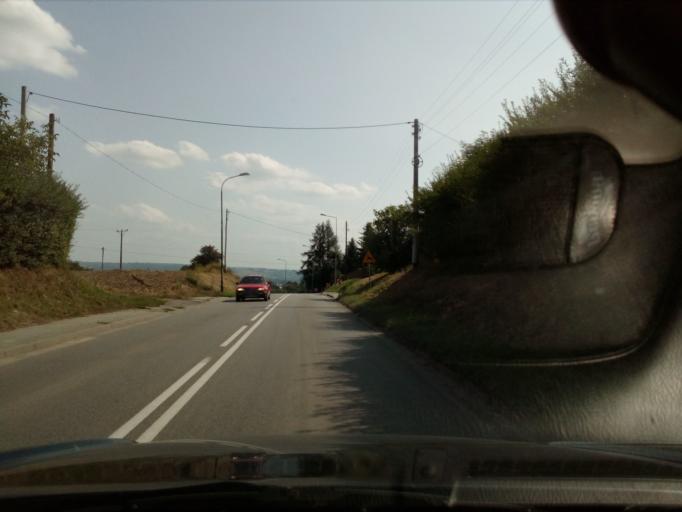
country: PL
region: Subcarpathian Voivodeship
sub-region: Powiat lancucki
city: Lancut
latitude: 50.0531
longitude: 22.2244
